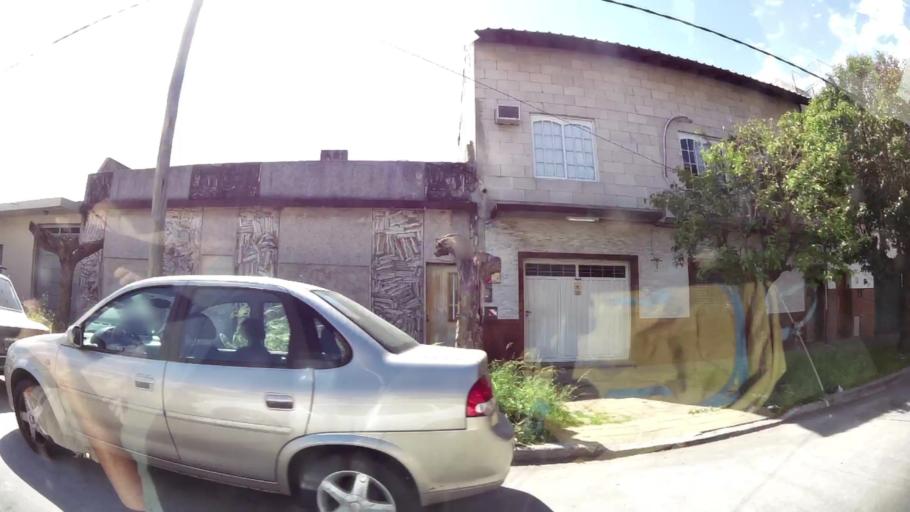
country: AR
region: Buenos Aires
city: San Justo
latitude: -34.6582
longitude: -58.5327
